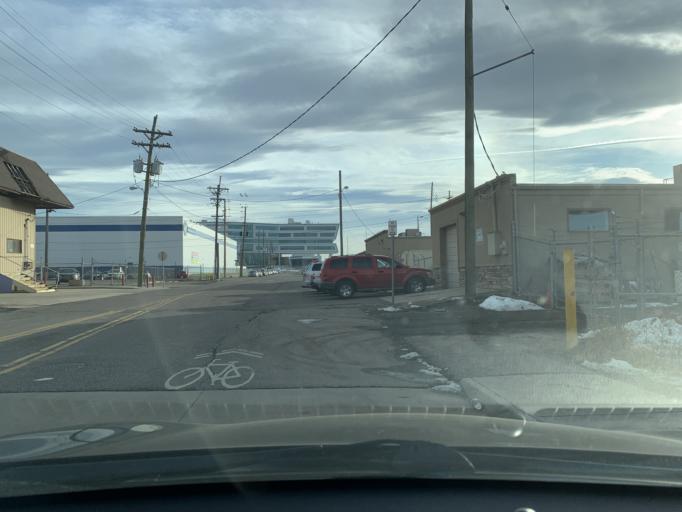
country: US
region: Colorado
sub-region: Denver County
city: Denver
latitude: 39.7377
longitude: -105.0105
